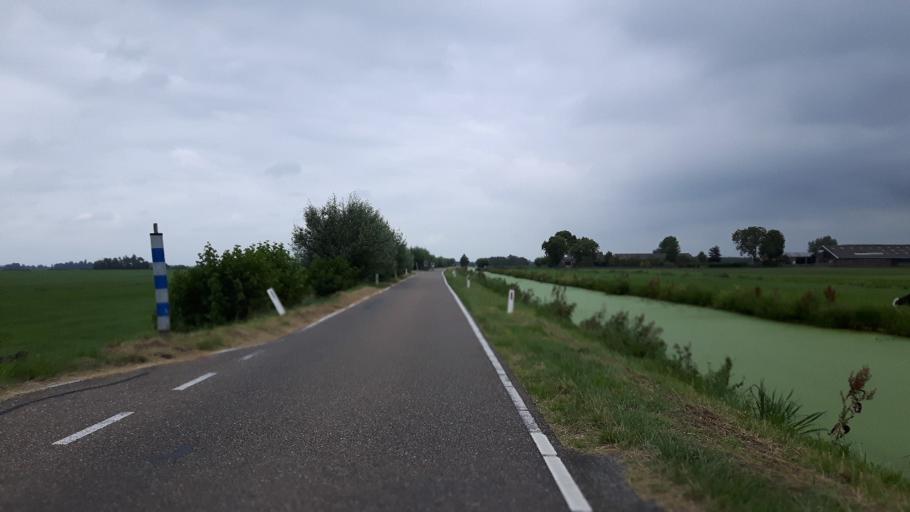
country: NL
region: South Holland
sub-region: Bodegraven-Reeuwijk
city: Bodegraven
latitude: 52.1100
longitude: 4.7426
